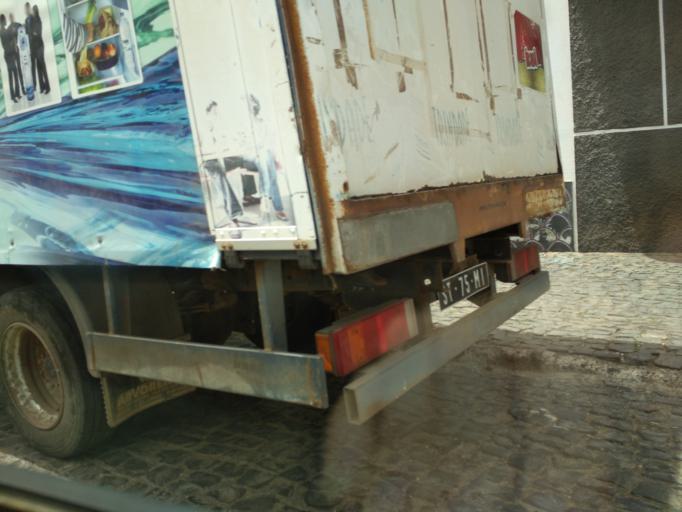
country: CV
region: Sal
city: Espargos
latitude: 16.7595
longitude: -22.9806
